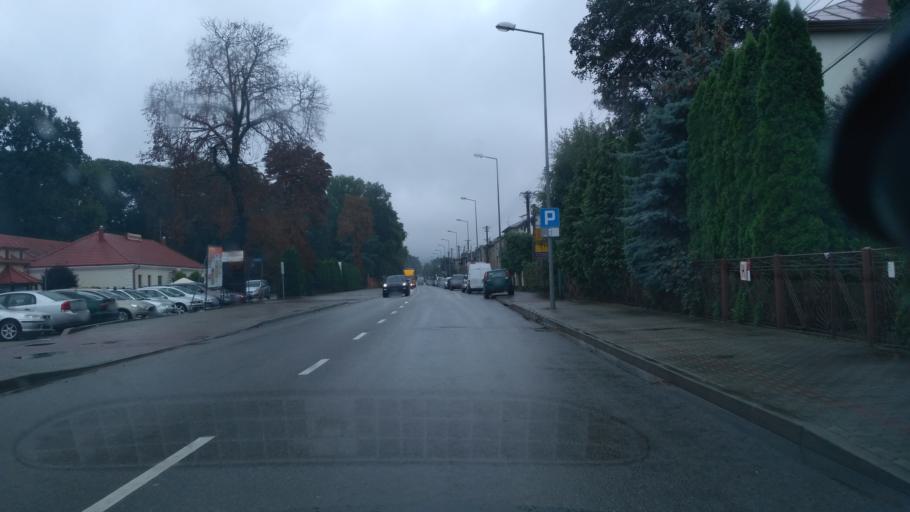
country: PL
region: Subcarpathian Voivodeship
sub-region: Powiat debicki
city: Debica
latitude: 50.0622
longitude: 21.4056
